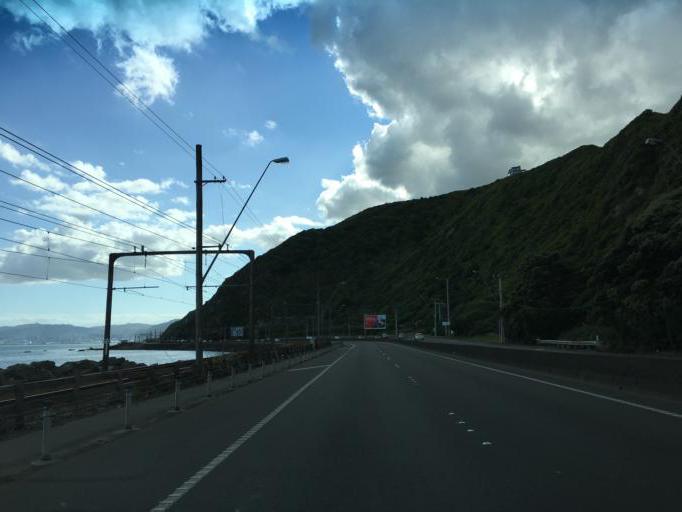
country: NZ
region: Wellington
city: Petone
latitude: -41.2281
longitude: 174.8460
